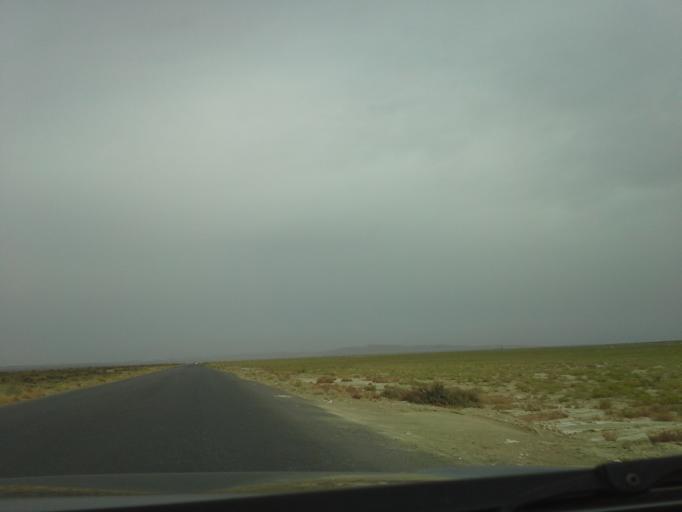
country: TM
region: Lebap
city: Atamyrat
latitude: 37.7346
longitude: 65.4971
